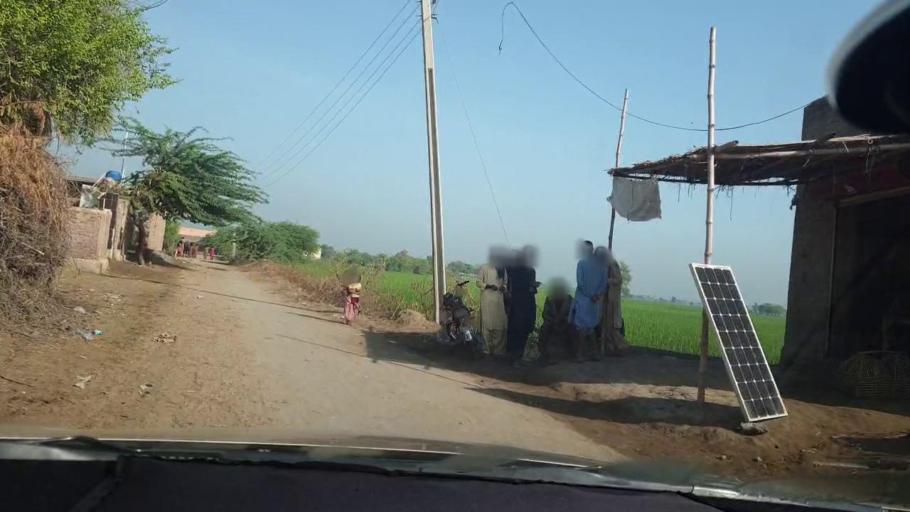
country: PK
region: Sindh
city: Kambar
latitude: 27.6637
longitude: 68.0135
